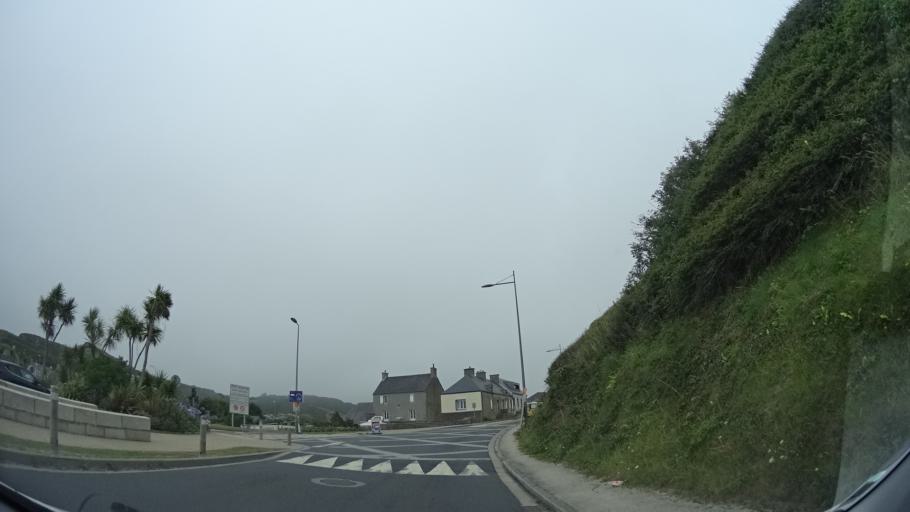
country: FR
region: Lower Normandy
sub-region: Departement de la Manche
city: Flamanville
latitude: 49.5510
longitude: -1.8584
